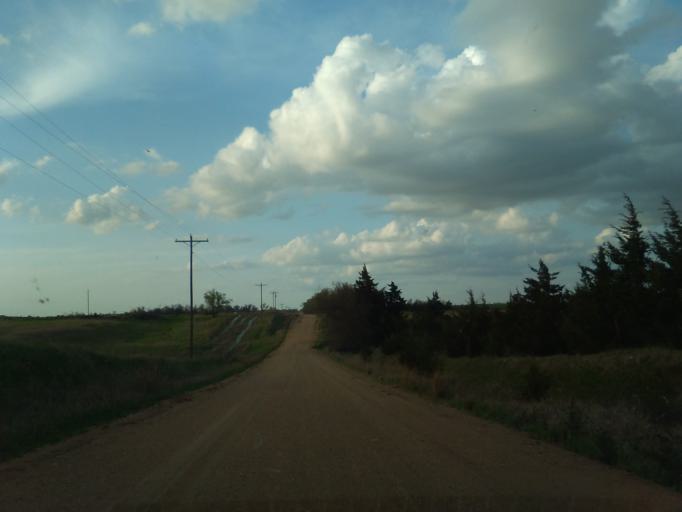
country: US
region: Nebraska
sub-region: Webster County
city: Red Cloud
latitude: 40.1767
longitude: -98.4059
